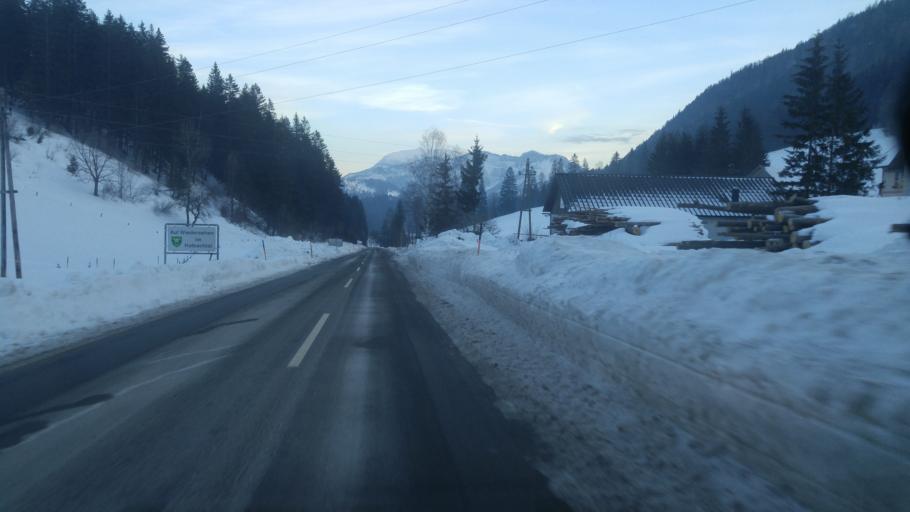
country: AT
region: Lower Austria
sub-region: Politischer Bezirk Wiener Neustadt
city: Rohr im Gebirge
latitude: 47.8862
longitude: 15.6849
